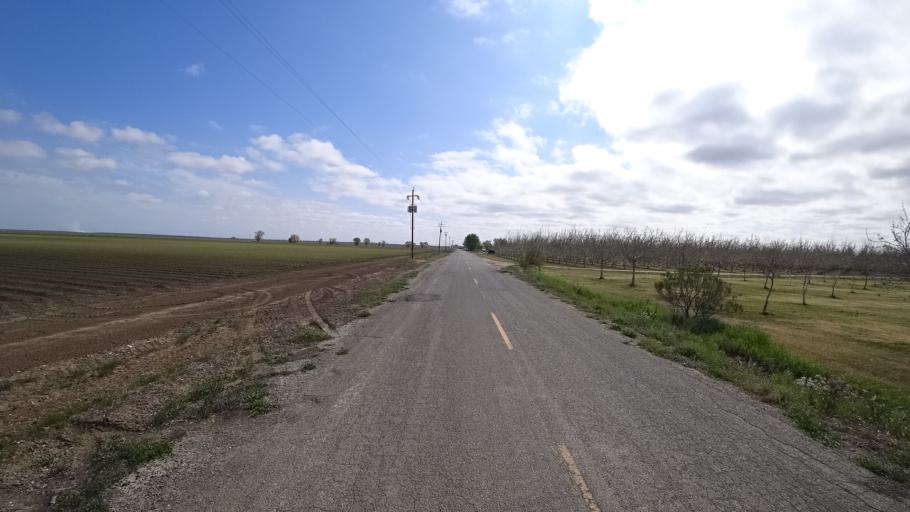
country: US
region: California
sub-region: Colusa County
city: Colusa
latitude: 39.4200
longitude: -121.9576
